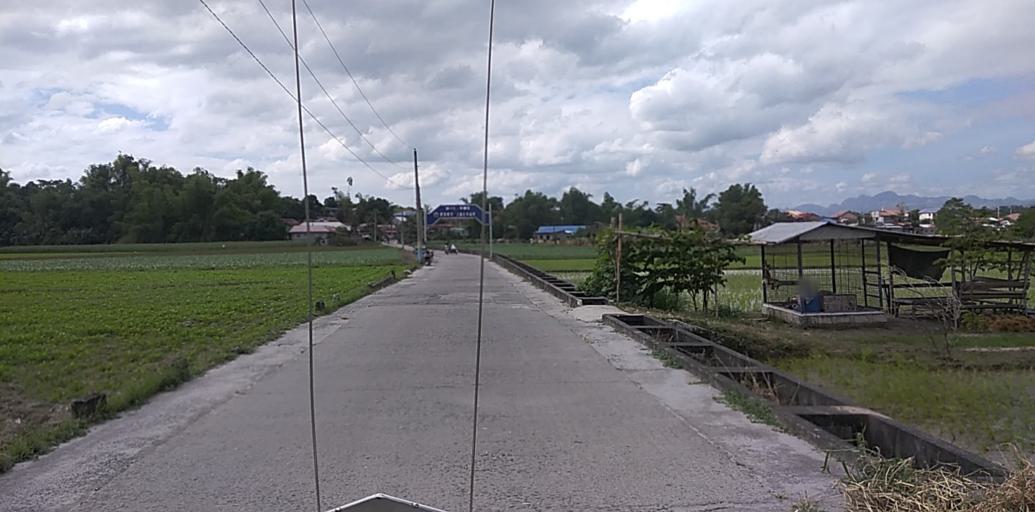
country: PH
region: Central Luzon
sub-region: Province of Pampanga
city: Porac
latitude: 15.0684
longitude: 120.5402
